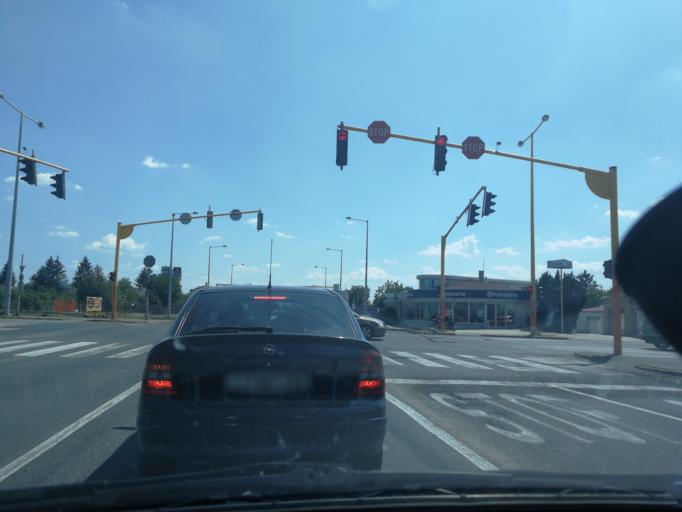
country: HU
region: Fejer
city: Szekesfehervar
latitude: 47.1951
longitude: 18.4453
